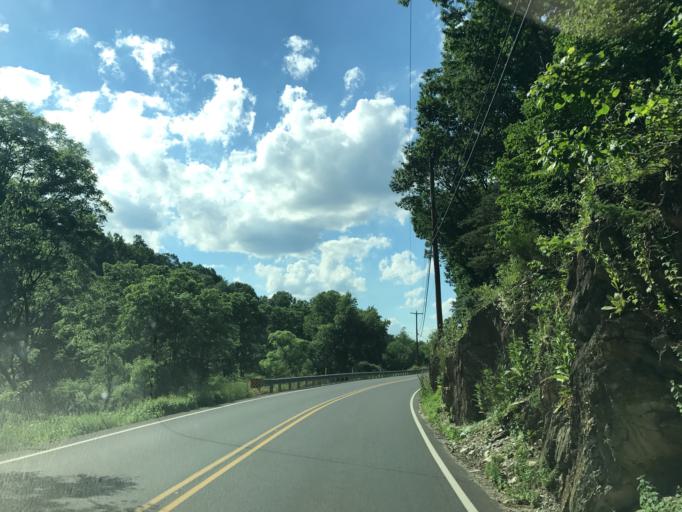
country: US
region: Pennsylvania
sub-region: York County
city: Glen Rock
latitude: 39.7622
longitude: -76.8199
